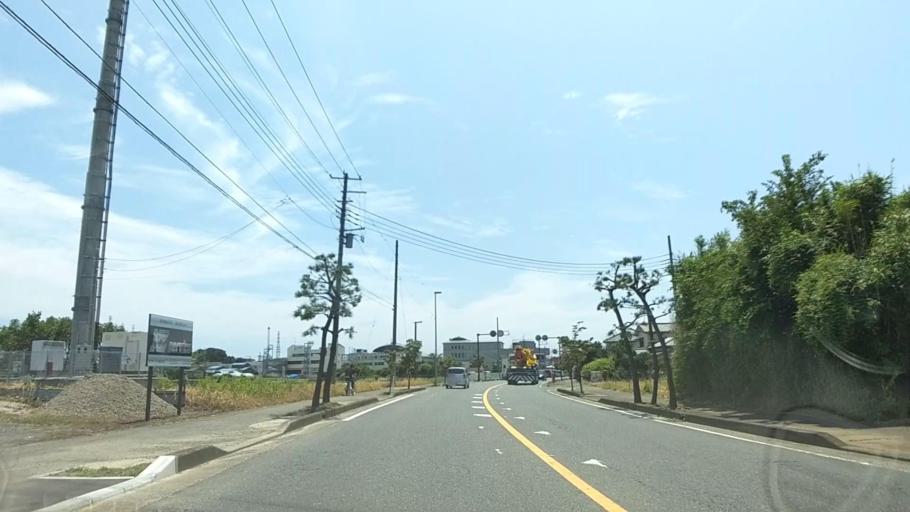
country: JP
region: Kanagawa
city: Chigasaki
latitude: 35.3794
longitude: 139.3856
